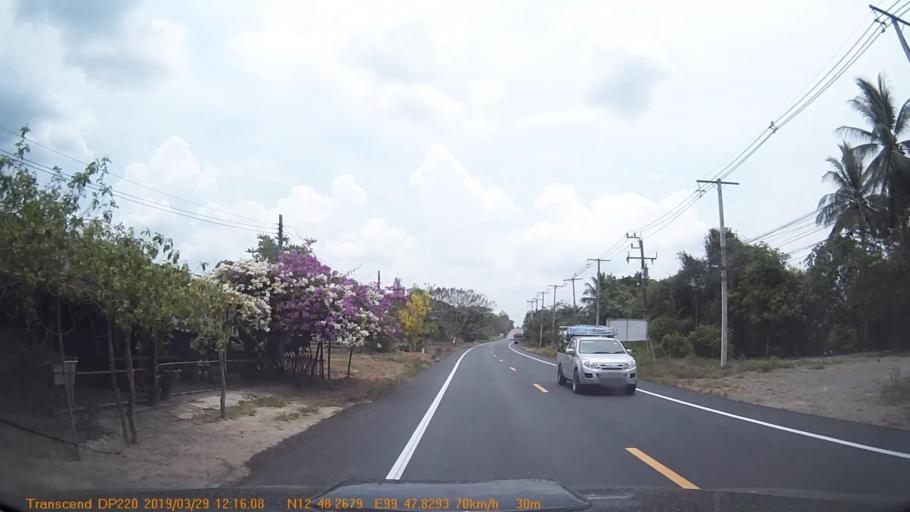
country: TH
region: Phetchaburi
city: Cha-am
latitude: 12.8042
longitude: 99.7972
